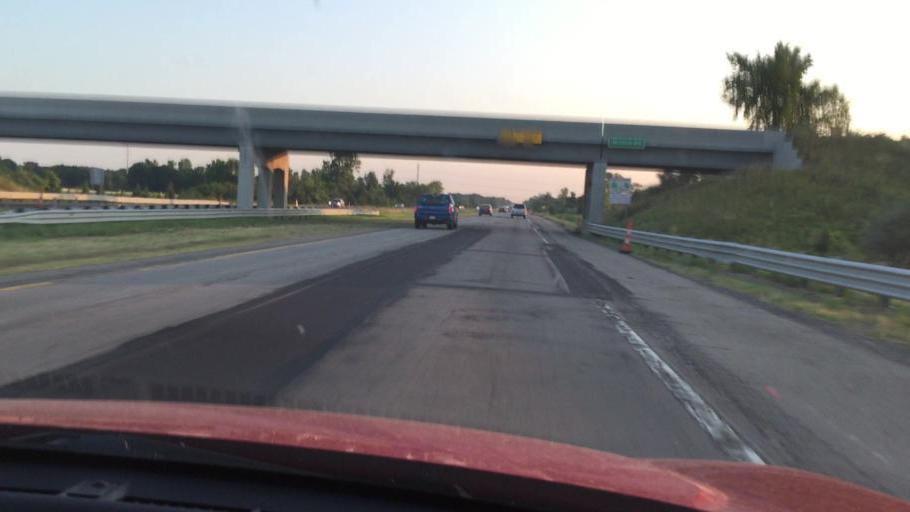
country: US
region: Michigan
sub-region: Washtenaw County
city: Milan
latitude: 42.1128
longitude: -83.6823
